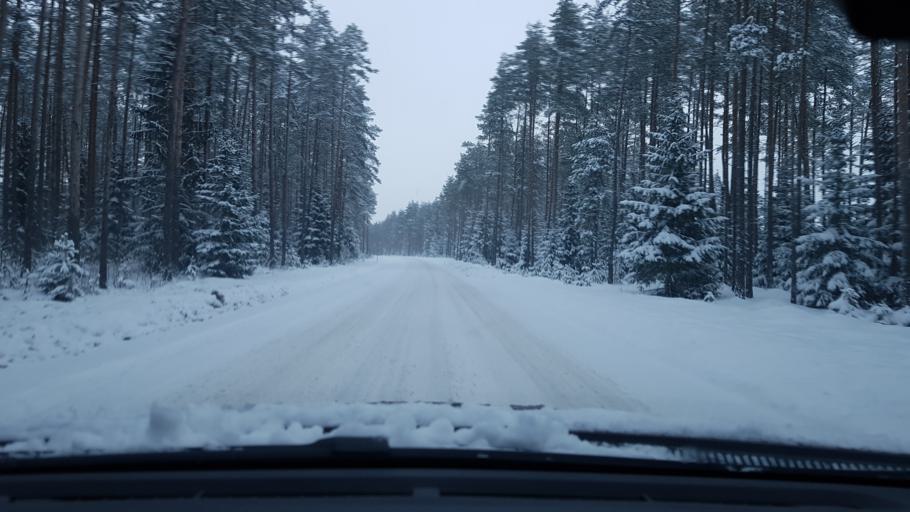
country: EE
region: Harju
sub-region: Anija vald
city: Kehra
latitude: 59.3981
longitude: 25.3733
